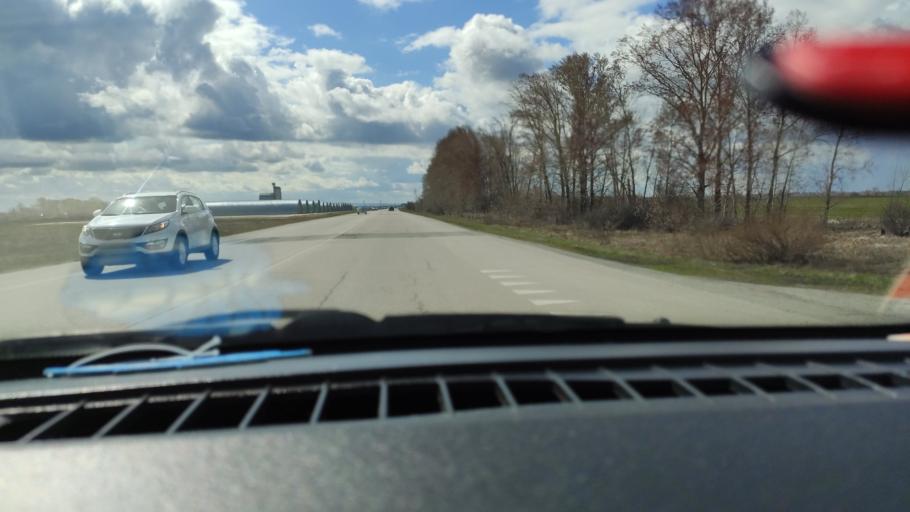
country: RU
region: Samara
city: Tol'yatti
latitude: 53.6886
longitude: 49.4177
